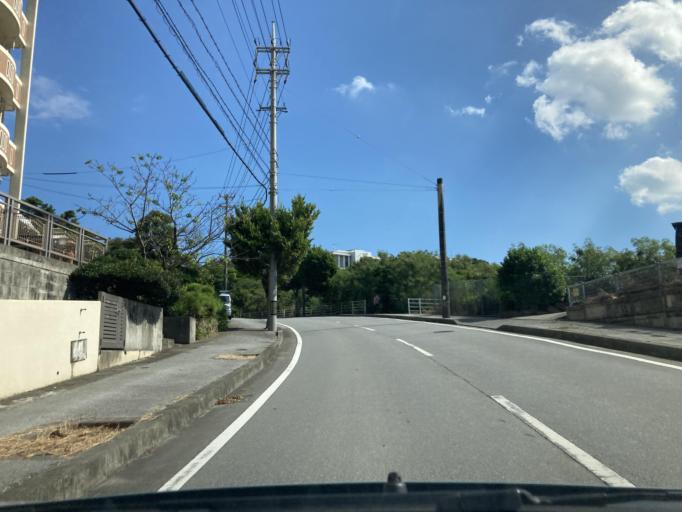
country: JP
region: Okinawa
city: Ginowan
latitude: 26.2440
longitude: 127.7558
